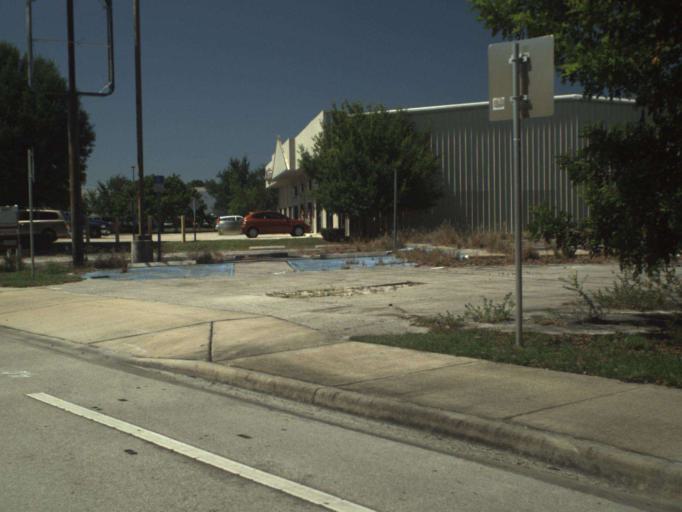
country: US
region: Florida
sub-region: Indian River County
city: Vero Beach South
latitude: 27.6127
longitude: -80.3860
